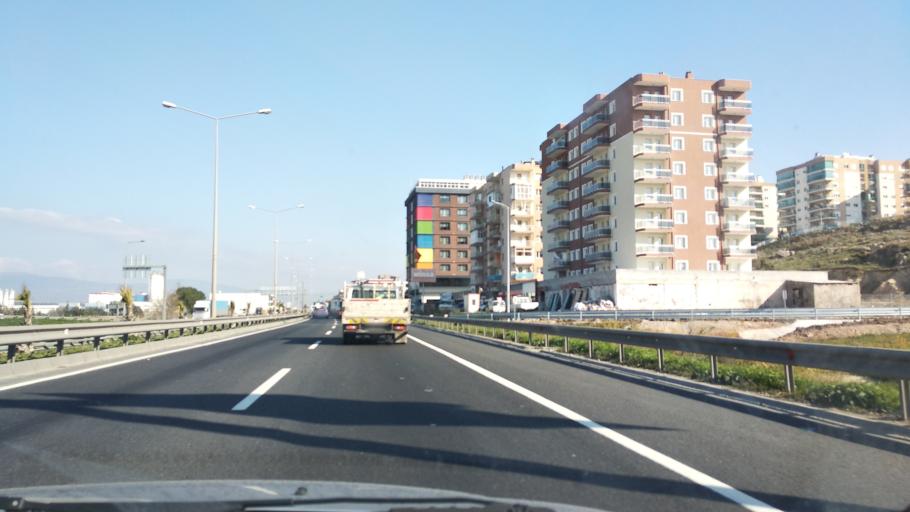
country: TR
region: Izmir
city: Menemen
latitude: 38.5717
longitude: 27.0581
